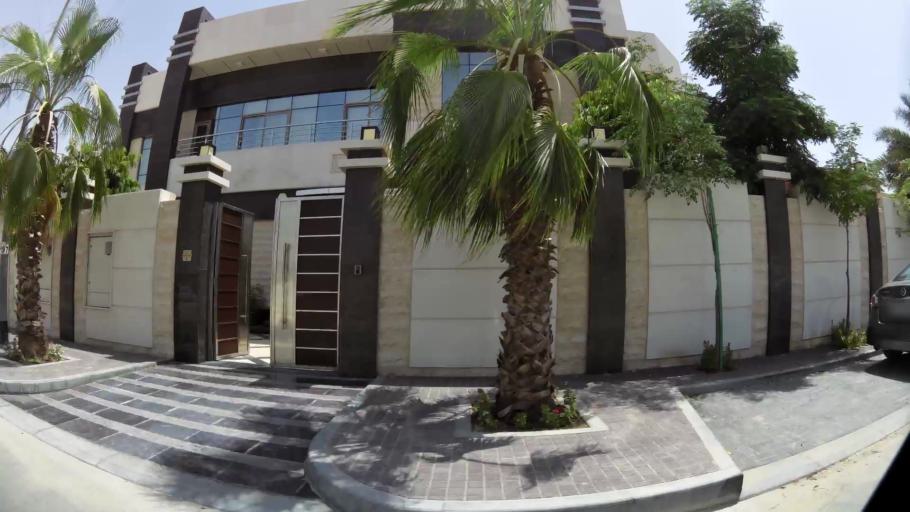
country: AE
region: Dubai
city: Dubai
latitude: 25.1383
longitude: 55.2049
